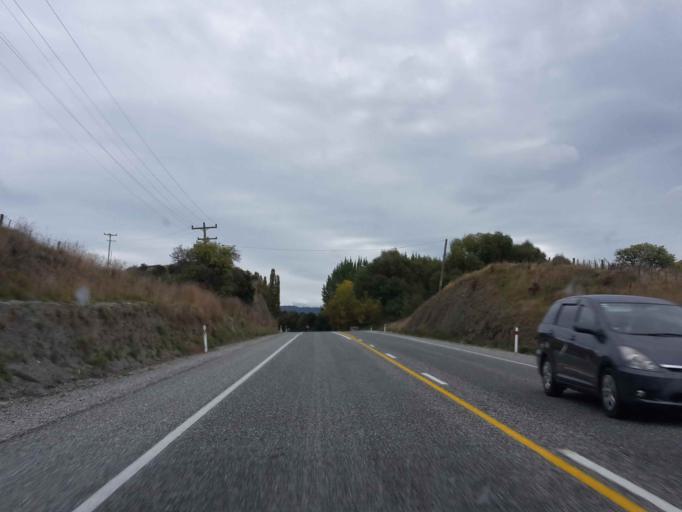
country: NZ
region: Otago
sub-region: Queenstown-Lakes District
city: Arrowtown
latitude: -44.9792
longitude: 168.8302
